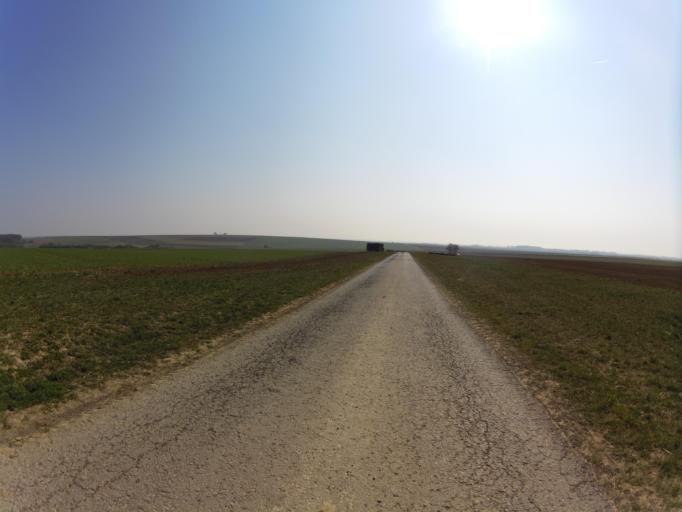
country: DE
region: Bavaria
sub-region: Regierungsbezirk Unterfranken
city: Eibelstadt
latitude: 49.6930
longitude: 9.9827
